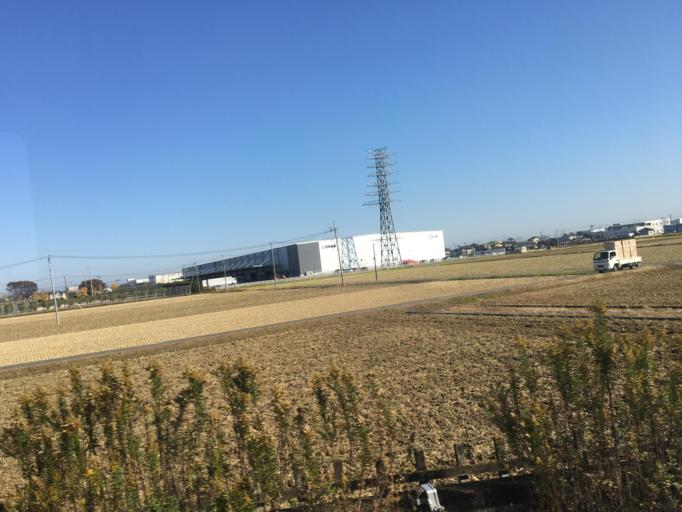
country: JP
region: Saitama
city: Hanyu
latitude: 36.1594
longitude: 139.5430
